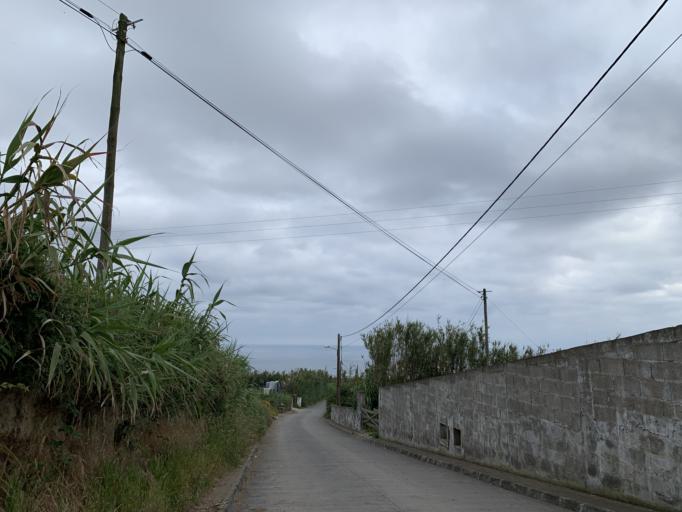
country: PT
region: Azores
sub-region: Ponta Delgada
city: Arrifes
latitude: 37.8549
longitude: -25.8474
